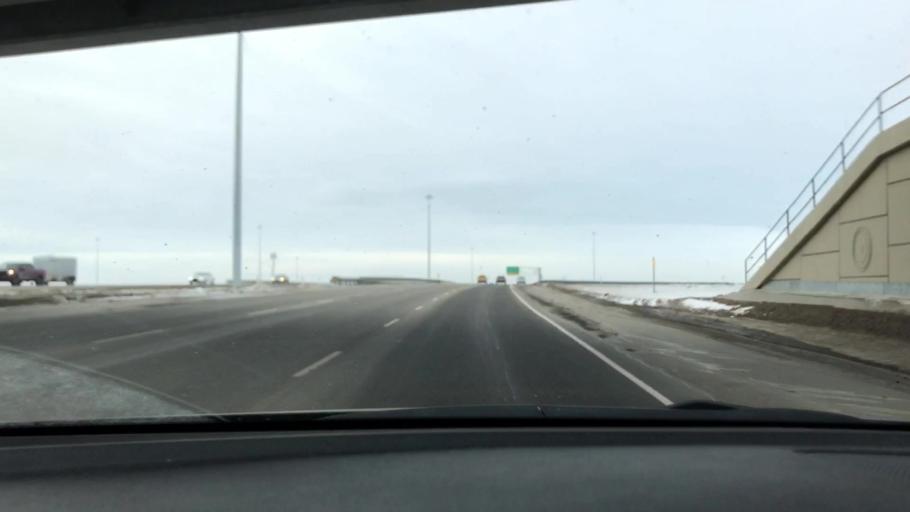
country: CA
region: Alberta
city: Sherwood Park
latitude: 53.5125
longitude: -113.3407
